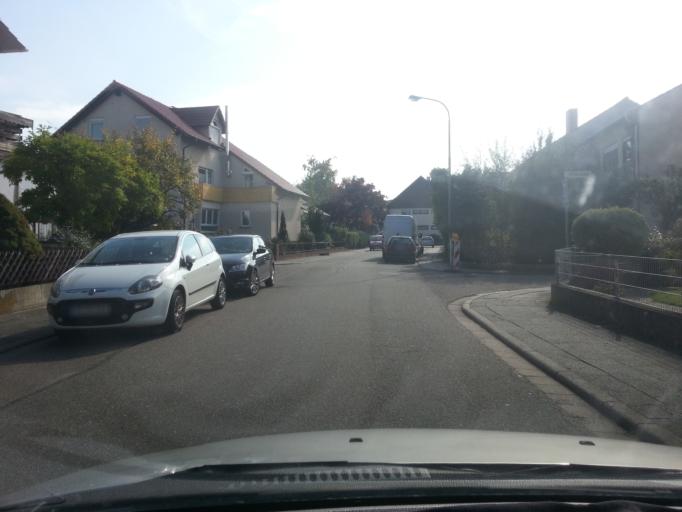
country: DE
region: Rheinland-Pfalz
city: Bohl-Iggelheim
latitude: 49.3605
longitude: 8.3048
